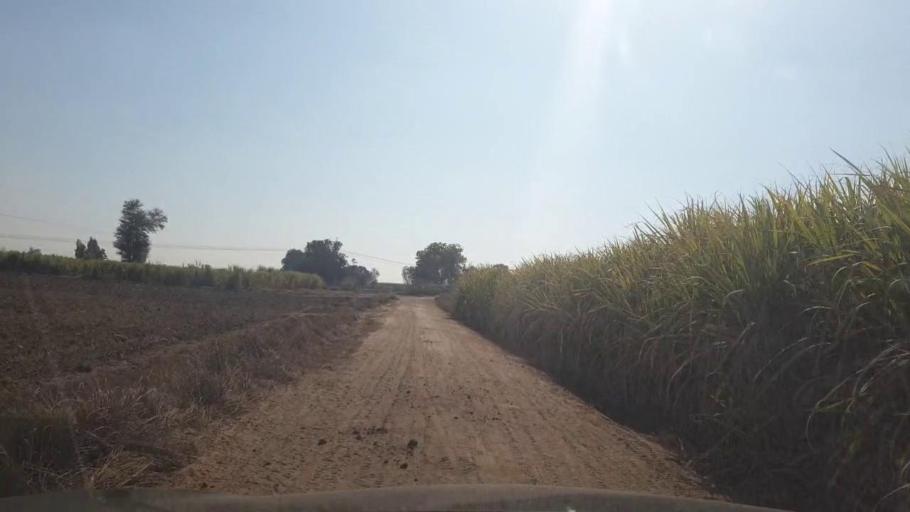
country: PK
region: Sindh
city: Adilpur
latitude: 27.9715
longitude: 69.4301
